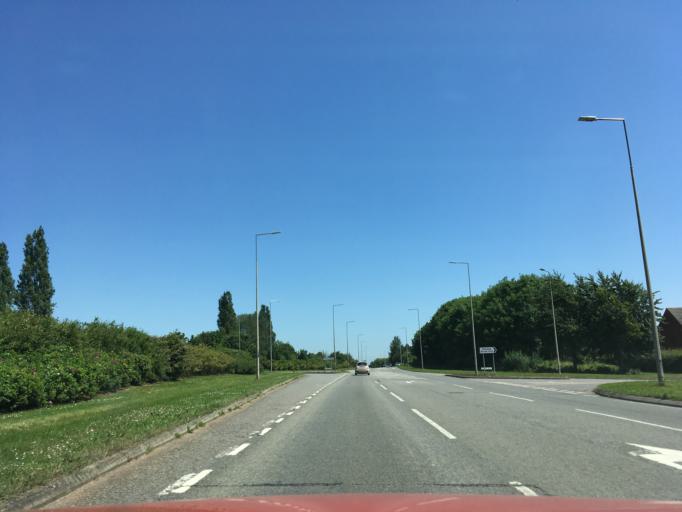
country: GB
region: England
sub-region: Milton Keynes
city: Shenley Church End
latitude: 52.0129
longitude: -0.7934
